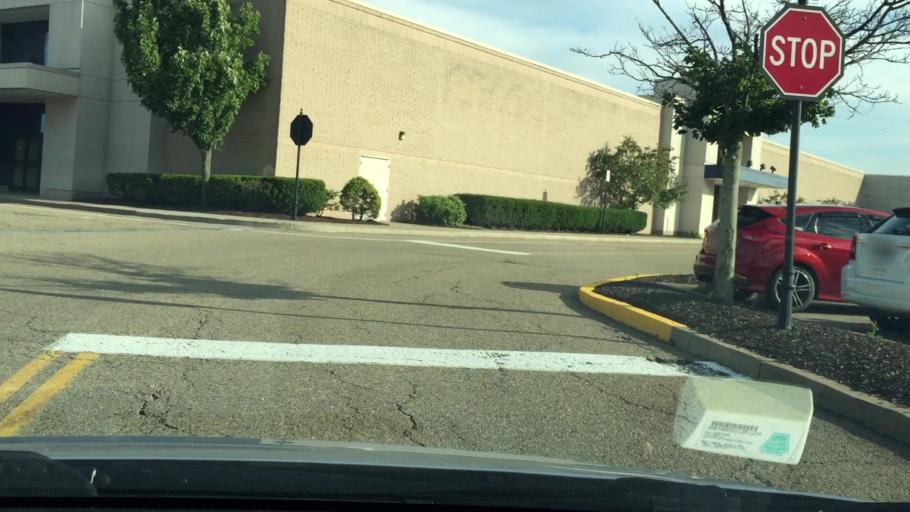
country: US
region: Pennsylvania
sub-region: Allegheny County
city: West View
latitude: 40.5457
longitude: -80.0069
